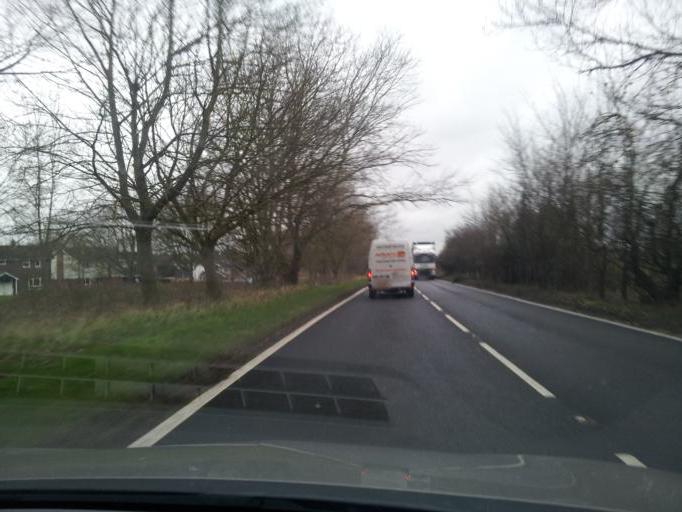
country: GB
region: England
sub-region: Suffolk
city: Ixworth
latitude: 52.3262
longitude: 0.8885
